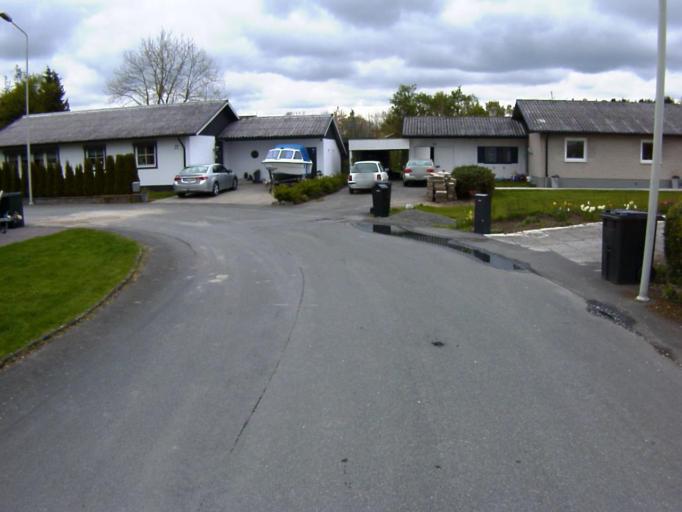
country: SE
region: Skane
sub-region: Kristianstads Kommun
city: Kristianstad
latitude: 56.0493
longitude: 14.1791
